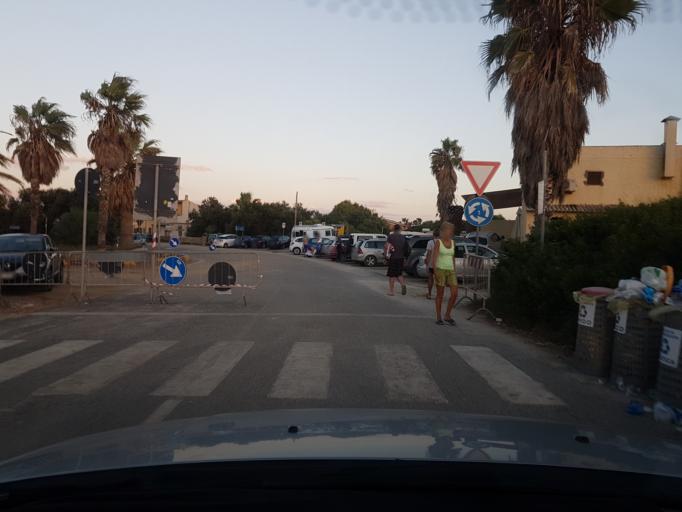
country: IT
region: Sardinia
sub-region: Provincia di Oristano
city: Riola Sardo
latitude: 40.0286
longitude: 8.4077
